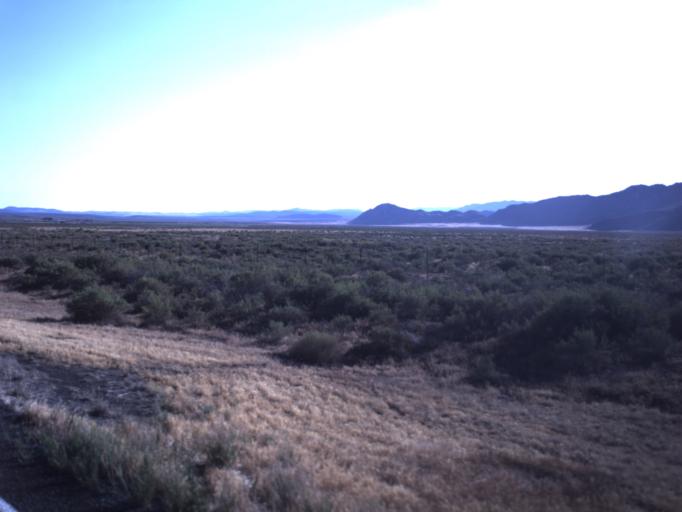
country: US
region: Utah
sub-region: Iron County
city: Enoch
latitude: 37.8660
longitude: -113.0316
